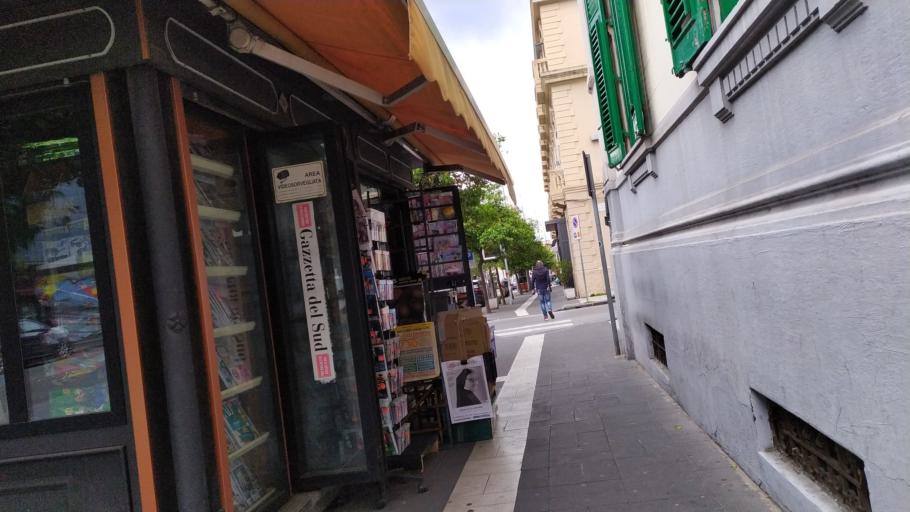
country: IT
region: Sicily
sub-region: Messina
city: Messina
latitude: 38.1877
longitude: 15.5545
